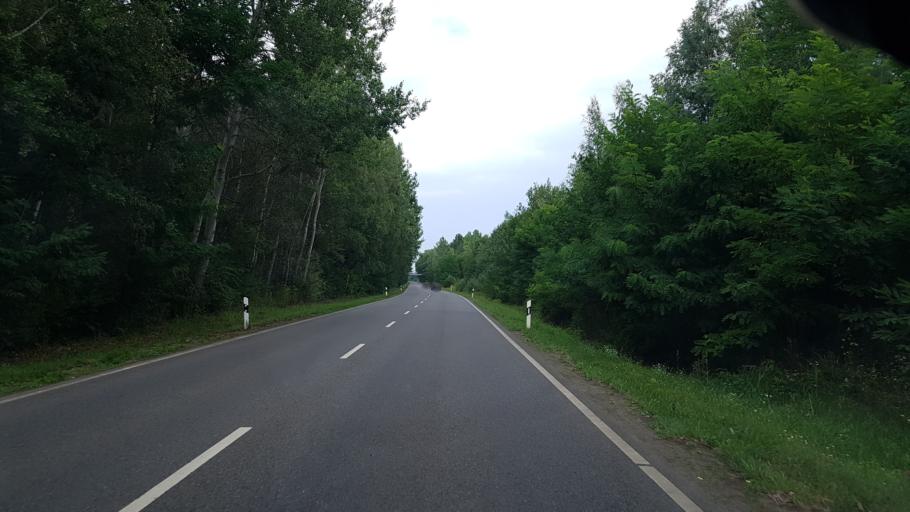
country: DE
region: Brandenburg
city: Lauchhammer
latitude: 51.4990
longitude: 13.7399
